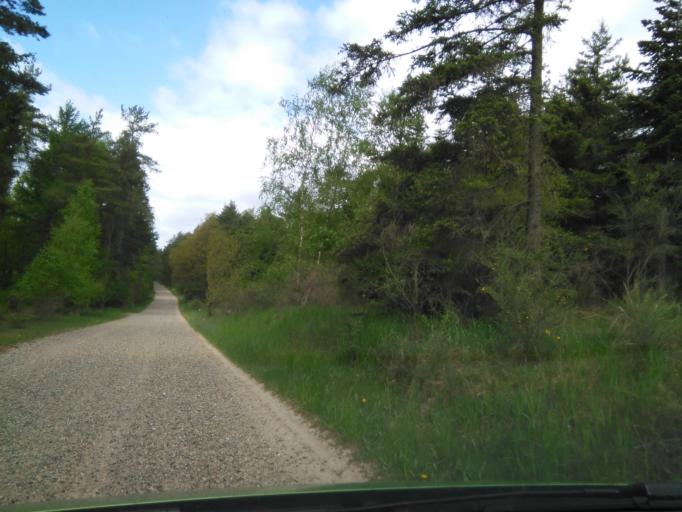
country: DK
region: Central Jutland
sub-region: Skanderborg Kommune
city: Ry
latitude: 56.0593
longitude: 9.7012
